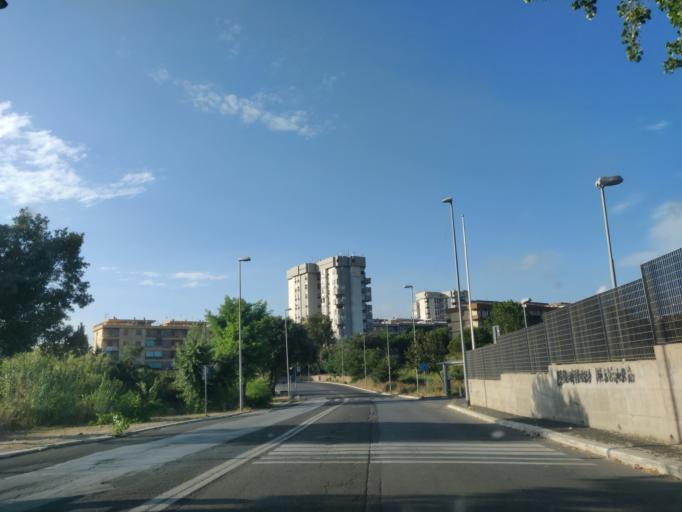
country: IT
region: Latium
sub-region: Citta metropolitana di Roma Capitale
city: Civitavecchia
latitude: 42.0798
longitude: 11.8141
